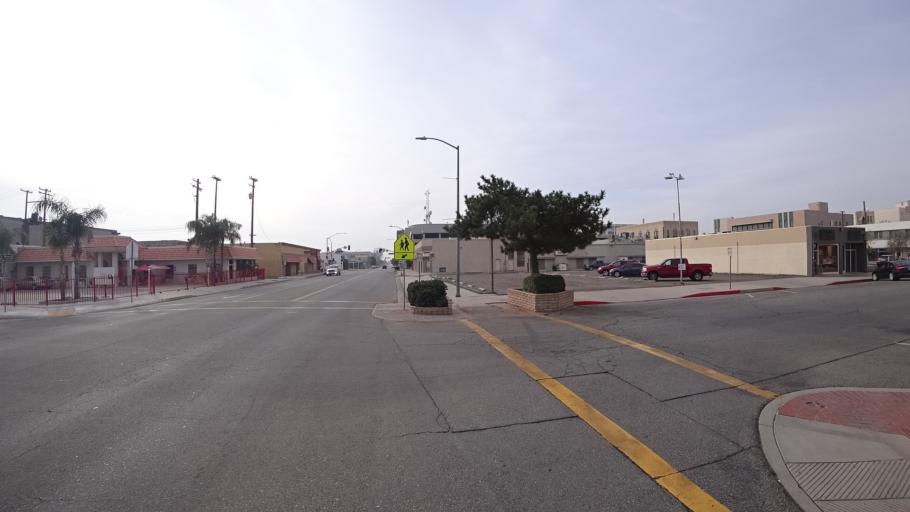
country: US
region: California
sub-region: Kern County
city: Bakersfield
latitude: 35.3773
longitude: -119.0165
